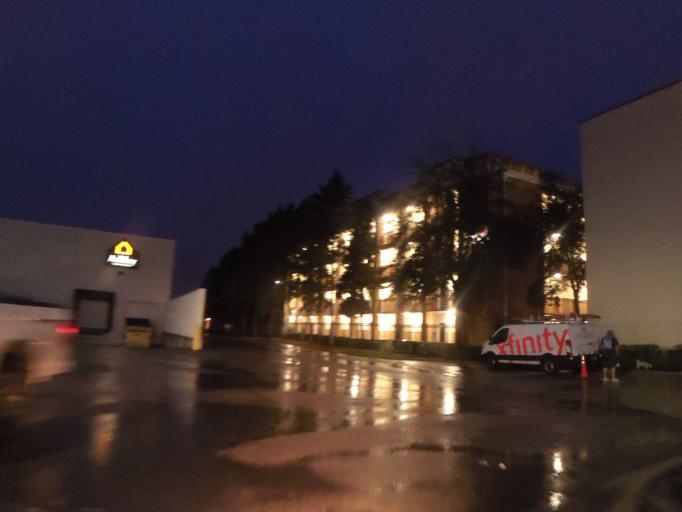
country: US
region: Florida
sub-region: Duval County
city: Jacksonville Beach
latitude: 30.2590
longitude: -81.5243
